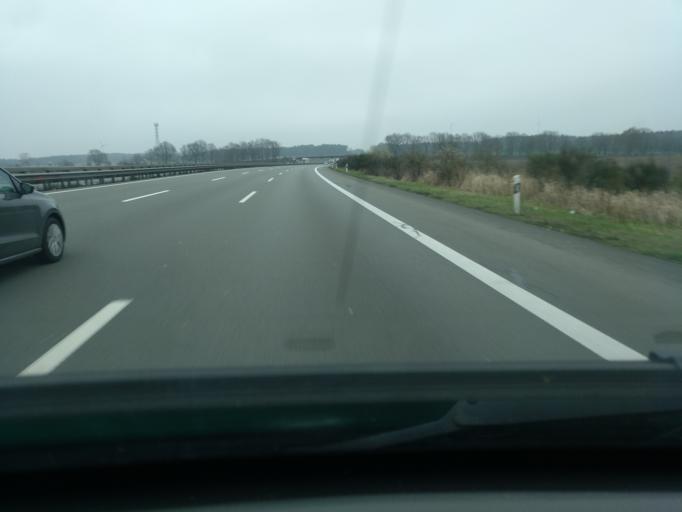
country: DE
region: Lower Saxony
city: Appel
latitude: 53.3689
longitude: 9.7506
